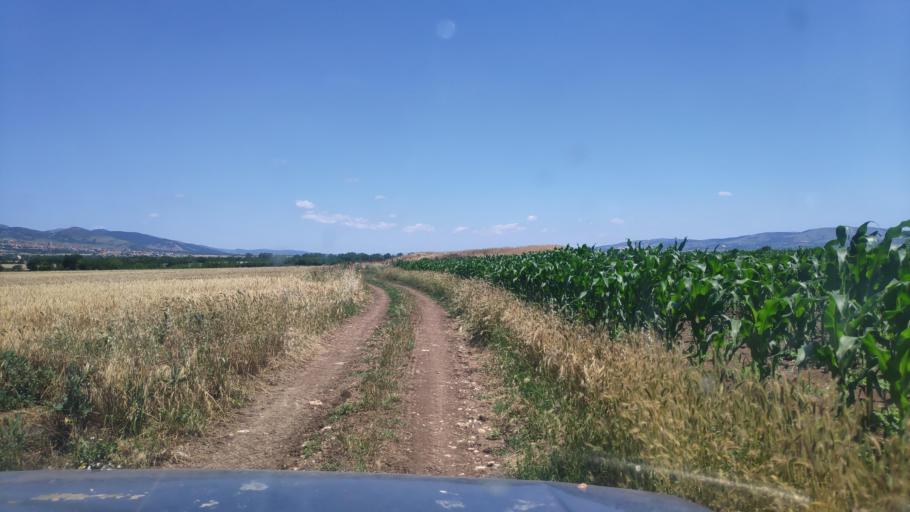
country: MK
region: Kumanovo
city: Bedinje
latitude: 42.1648
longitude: 21.6840
